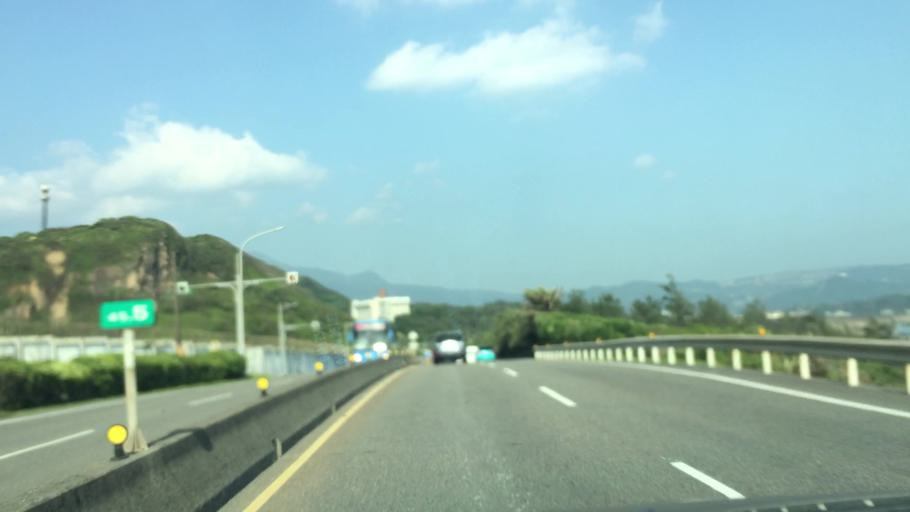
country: TW
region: Taiwan
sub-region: Keelung
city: Keelung
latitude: 25.2058
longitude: 121.6639
